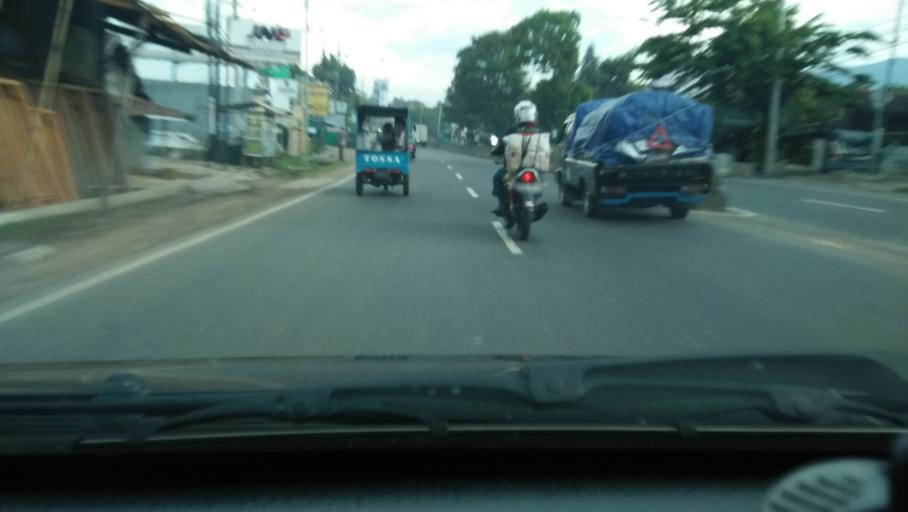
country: ID
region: Central Java
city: Ungaran
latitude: -7.1011
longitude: 110.4091
